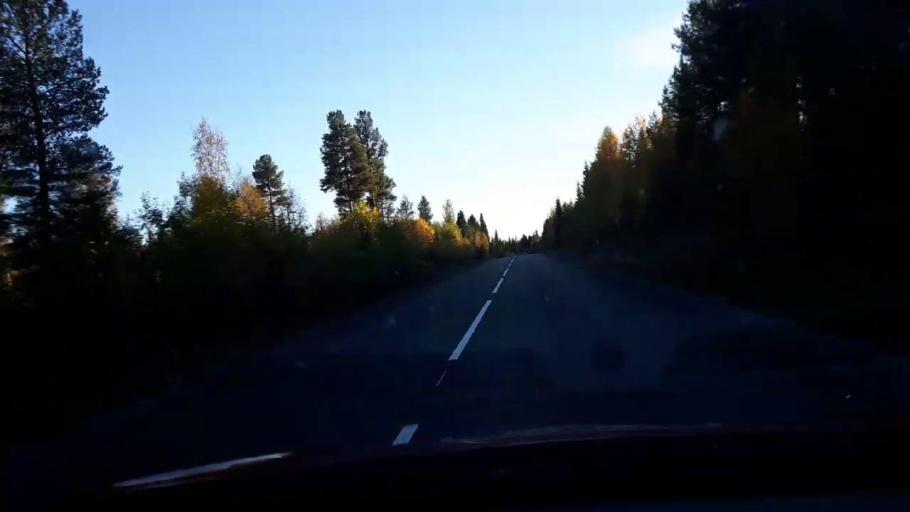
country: SE
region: Jaemtland
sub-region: OEstersunds Kommun
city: Lit
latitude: 63.4599
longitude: 14.8508
